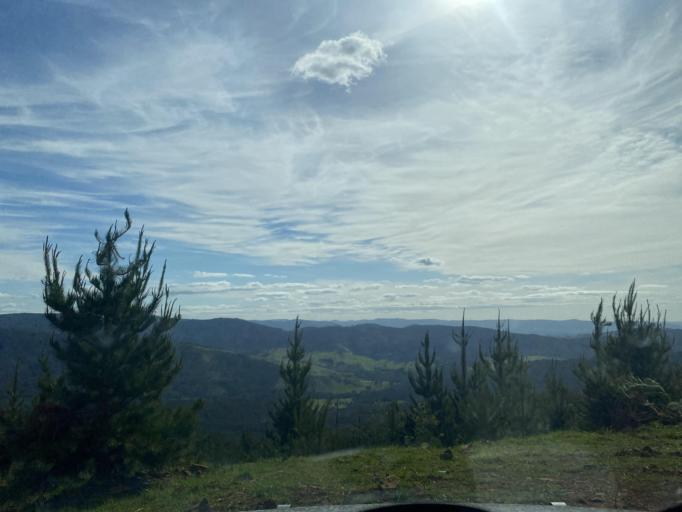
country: AU
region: Victoria
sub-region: Mansfield
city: Mansfield
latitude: -36.8330
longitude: 146.1781
